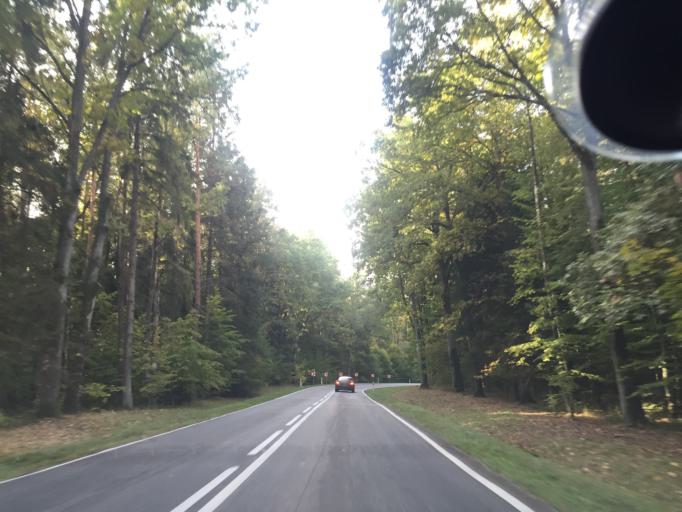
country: PL
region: Warmian-Masurian Voivodeship
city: Dobre Miasto
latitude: 54.0365
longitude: 20.4283
